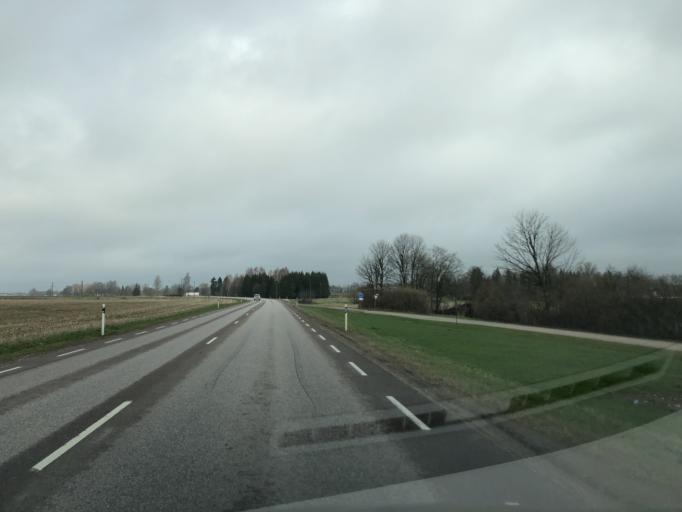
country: EE
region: Jogevamaa
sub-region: Jogeva linn
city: Jogeva
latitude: 58.7196
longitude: 26.3959
